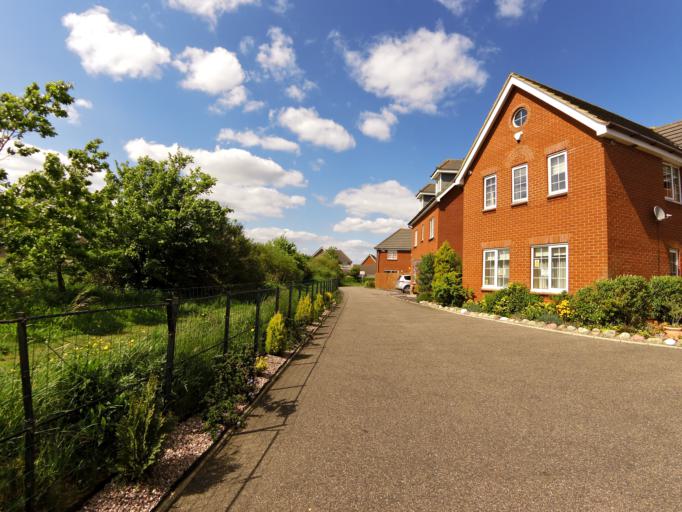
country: GB
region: England
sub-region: Suffolk
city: Kessingland
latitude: 52.4478
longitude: 1.7079
